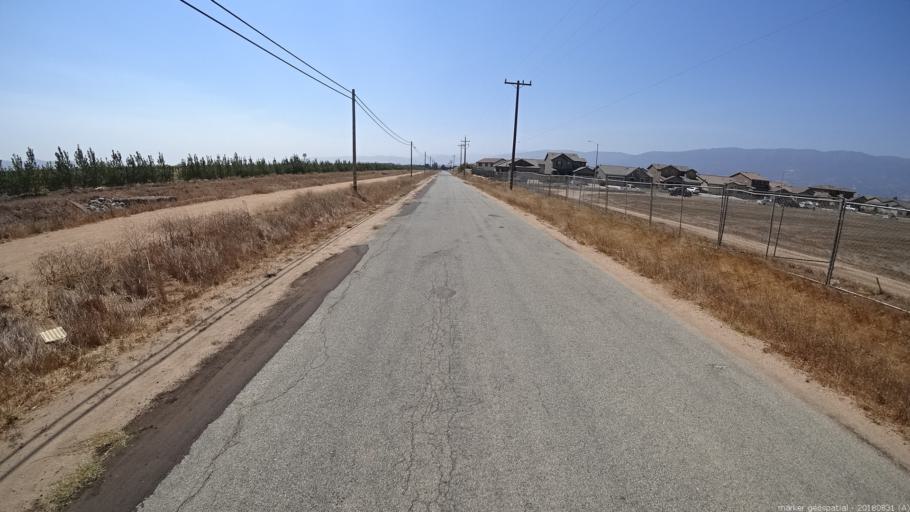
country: US
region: California
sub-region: Monterey County
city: Soledad
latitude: 36.4363
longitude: -121.3119
